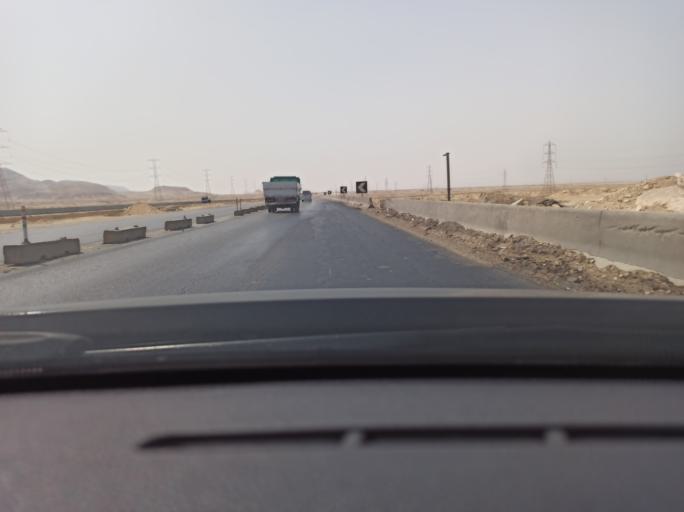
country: EG
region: Muhafazat Bani Suwayf
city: Bush
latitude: 29.1309
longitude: 31.2245
